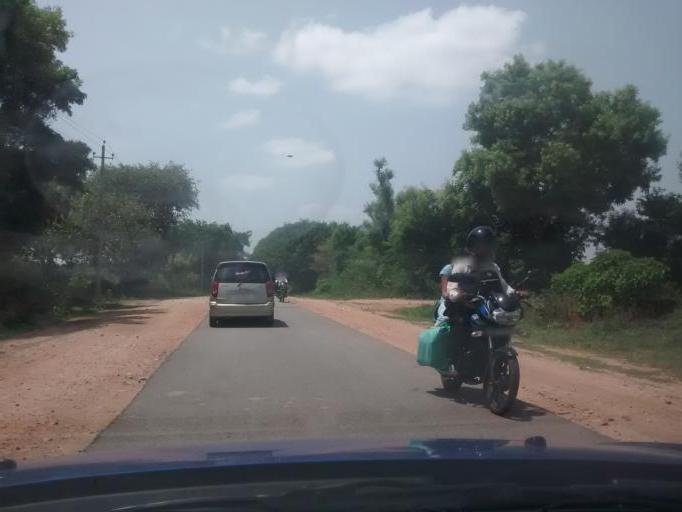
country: IN
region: Karnataka
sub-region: Hassan
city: Konanur
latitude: 12.5710
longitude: 76.2348
